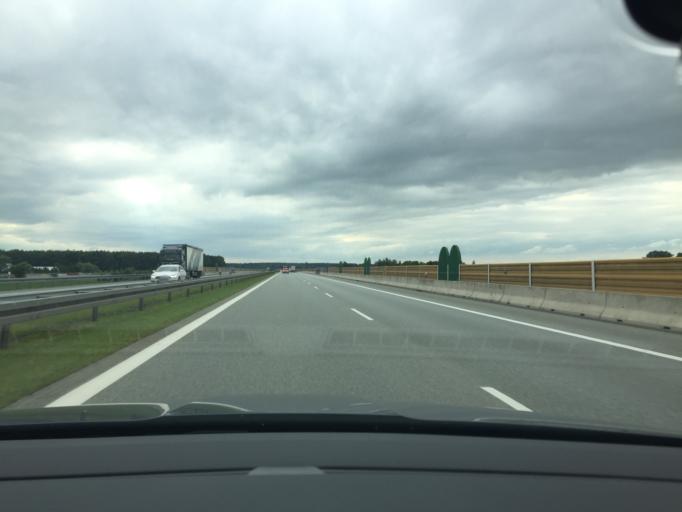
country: PL
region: Greater Poland Voivodeship
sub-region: Powiat poznanski
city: Dopiewo
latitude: 52.3502
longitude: 16.6587
